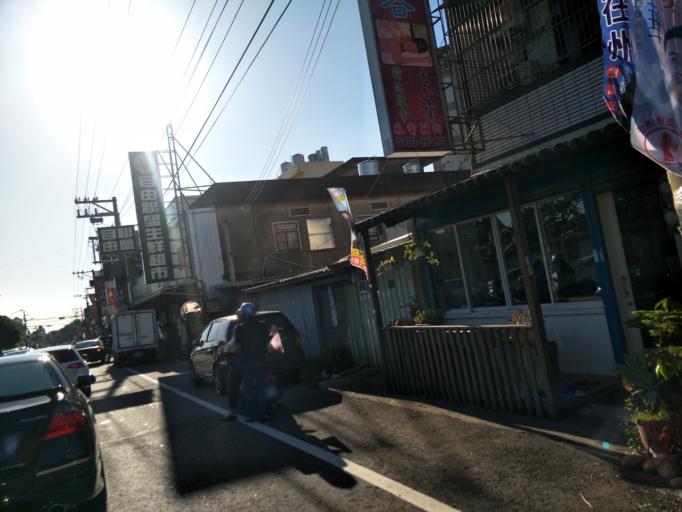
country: TW
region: Taiwan
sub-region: Hsinchu
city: Zhubei
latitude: 24.8640
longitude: 121.0275
